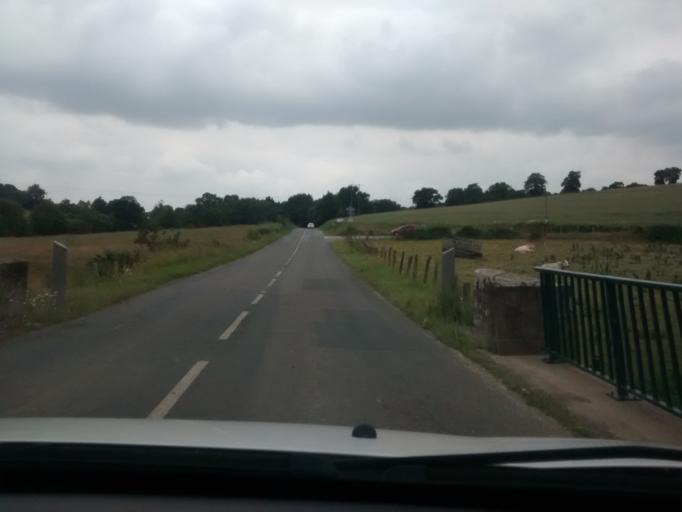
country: FR
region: Brittany
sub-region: Departement d'Ille-et-Vilaine
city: La Bouexiere
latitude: 48.1965
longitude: -1.4681
